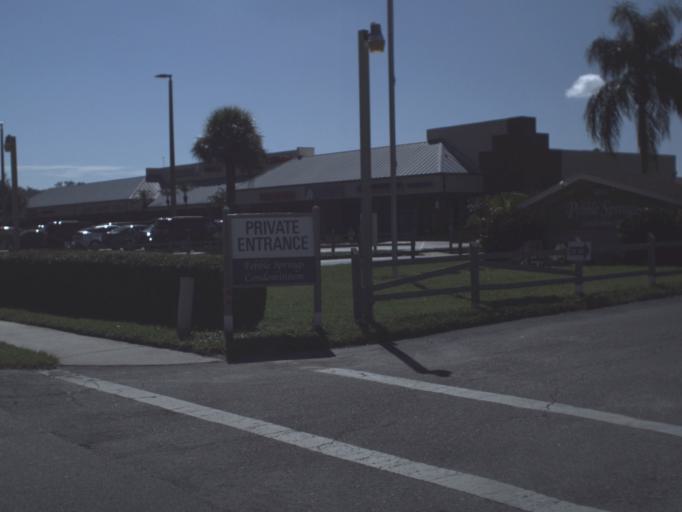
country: US
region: Florida
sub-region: Manatee County
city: West Bradenton
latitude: 27.4959
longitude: -82.6236
